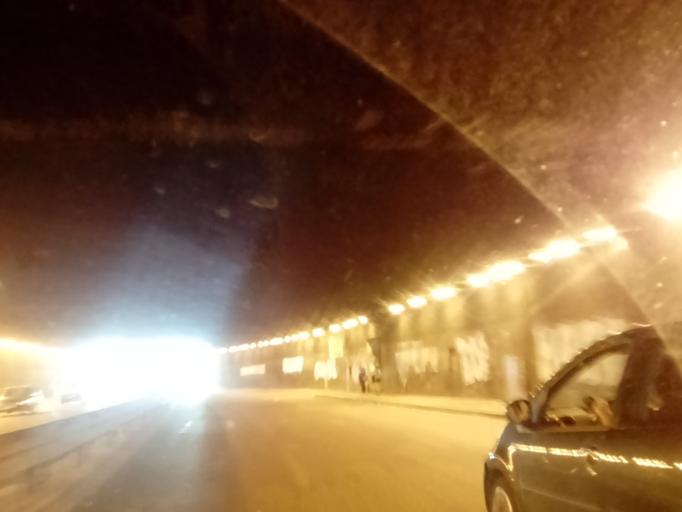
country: IT
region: Latium
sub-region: Citta metropolitana di Roma Capitale
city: Rome
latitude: 41.9110
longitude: 12.4934
